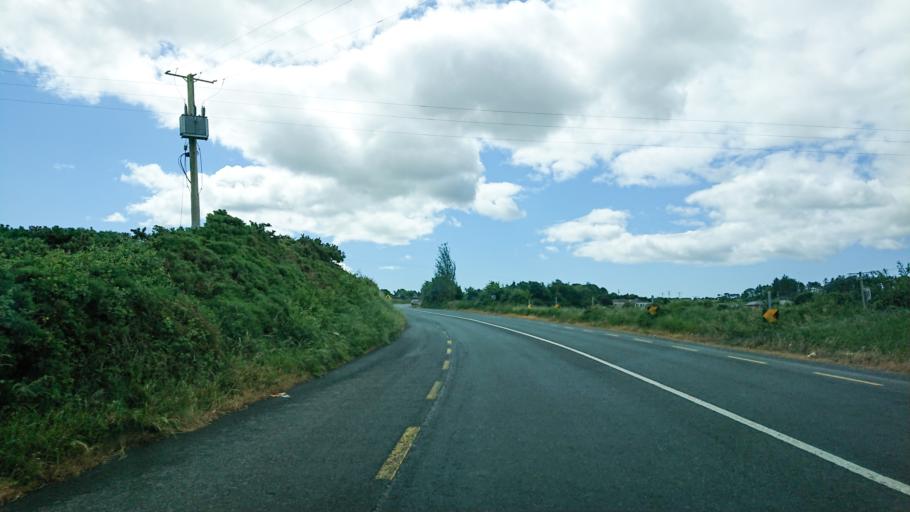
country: IE
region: Munster
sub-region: Waterford
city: Tra Mhor
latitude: 52.2248
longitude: -7.2003
